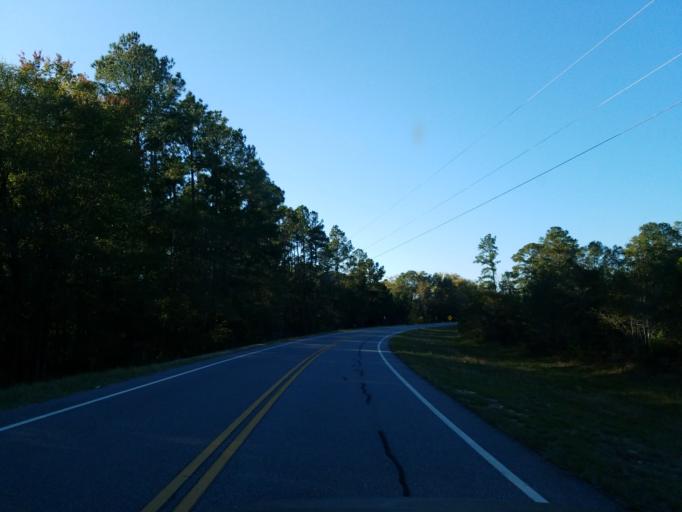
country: US
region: Georgia
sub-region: Lanier County
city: Lakeland
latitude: 30.9047
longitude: -83.0762
